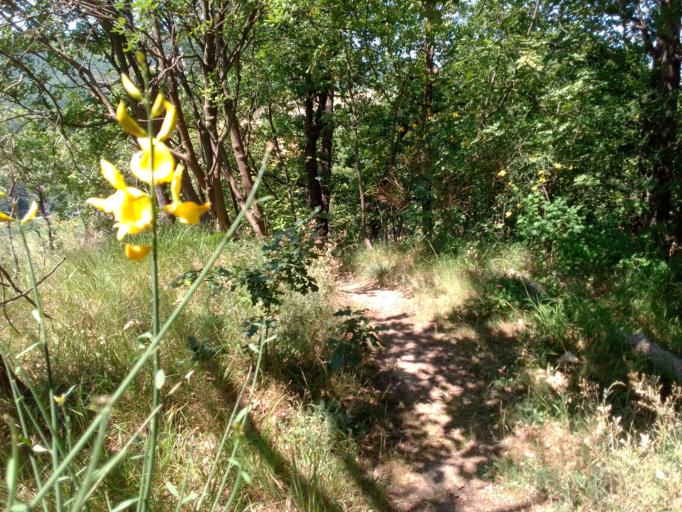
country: IT
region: Emilia-Romagna
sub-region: Provincia di Piacenza
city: Pecorara
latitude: 44.9074
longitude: 9.4027
